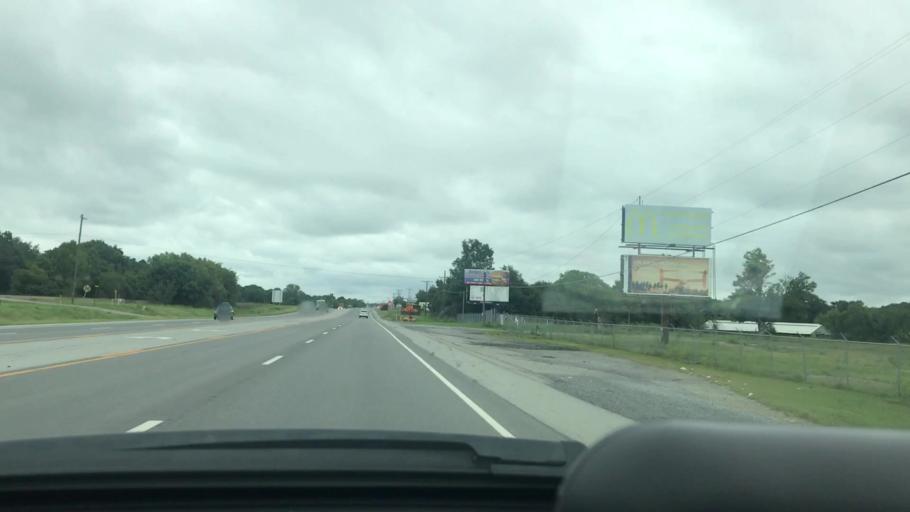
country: US
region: Oklahoma
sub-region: Pittsburg County
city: McAlester
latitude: 34.8756
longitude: -95.7989
